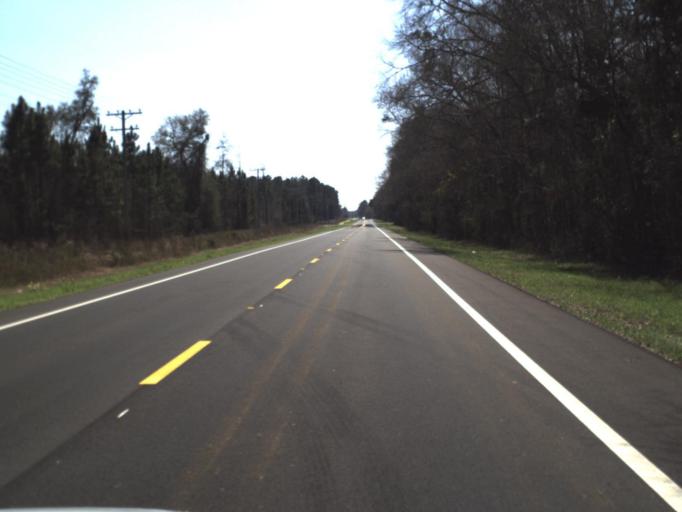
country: US
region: Florida
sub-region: Jackson County
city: Sneads
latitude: 30.7345
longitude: -85.0199
